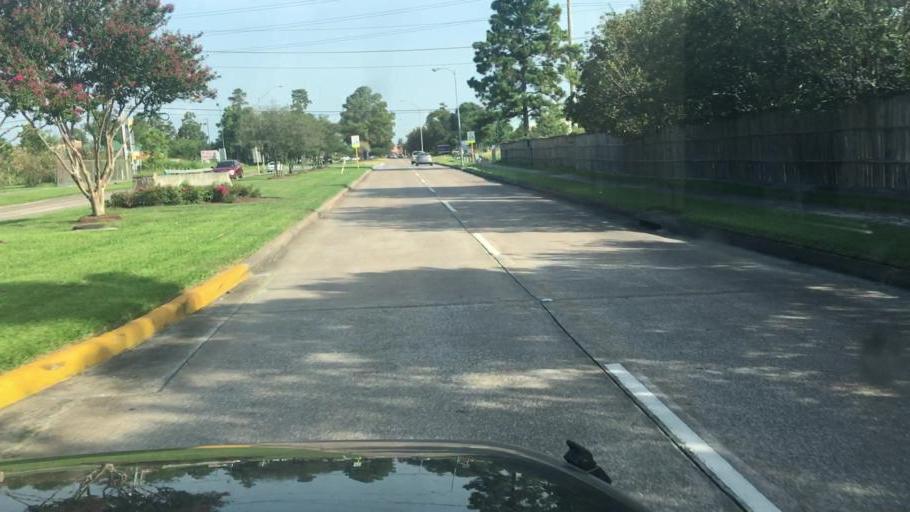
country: US
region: Texas
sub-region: Harris County
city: Atascocita
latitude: 30.0030
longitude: -95.1641
